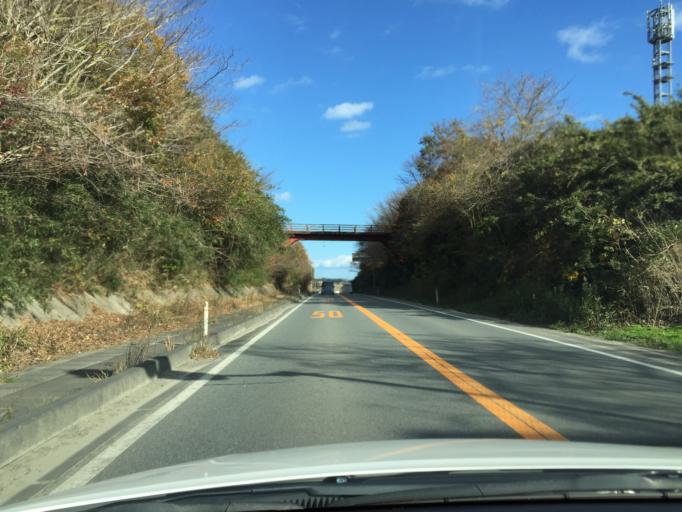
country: JP
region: Fukushima
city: Namie
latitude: 37.5736
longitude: 141.0071
